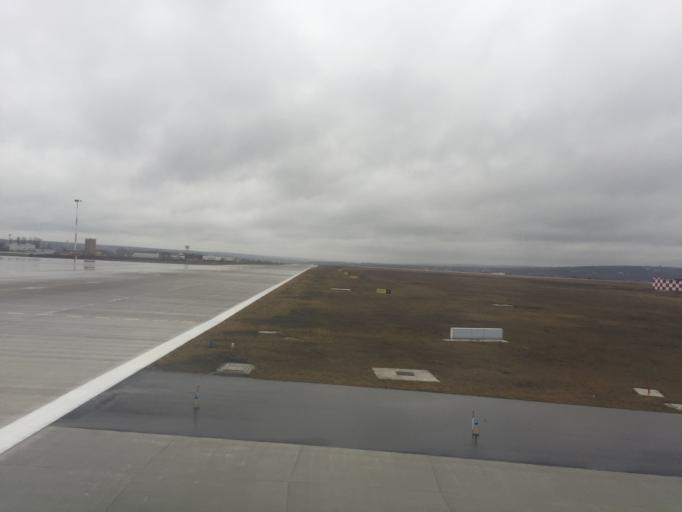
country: MD
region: Chisinau
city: Singera
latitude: 46.9311
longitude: 28.9344
